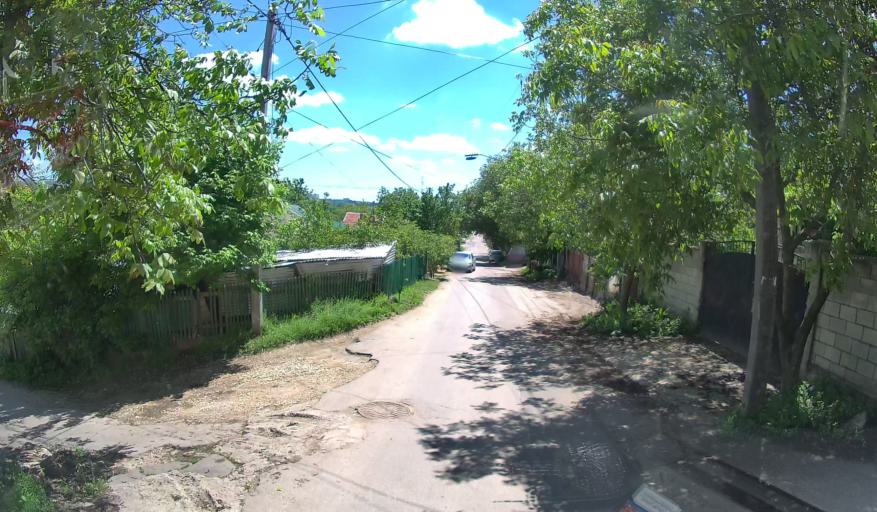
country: MD
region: Chisinau
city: Chisinau
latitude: 47.0511
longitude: 28.8327
